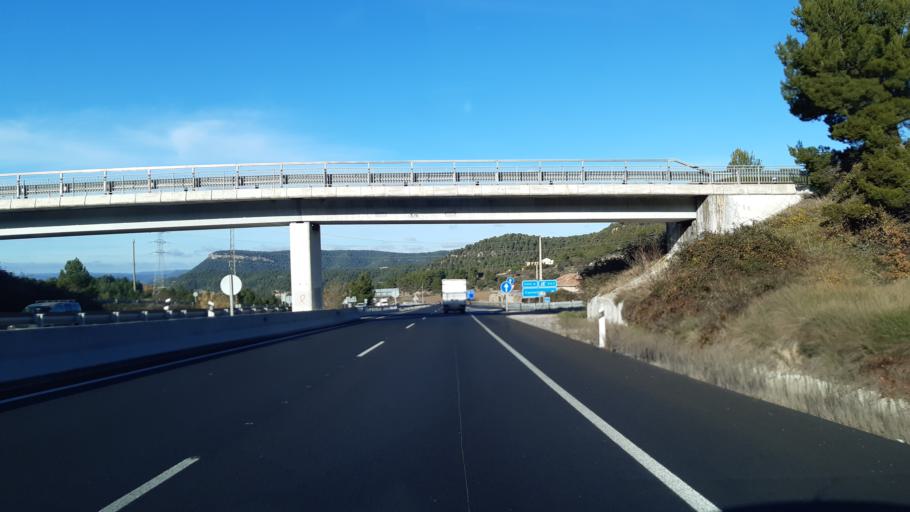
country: ES
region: Catalonia
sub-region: Provincia de Barcelona
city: Castelloli
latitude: 41.5953
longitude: 1.7209
